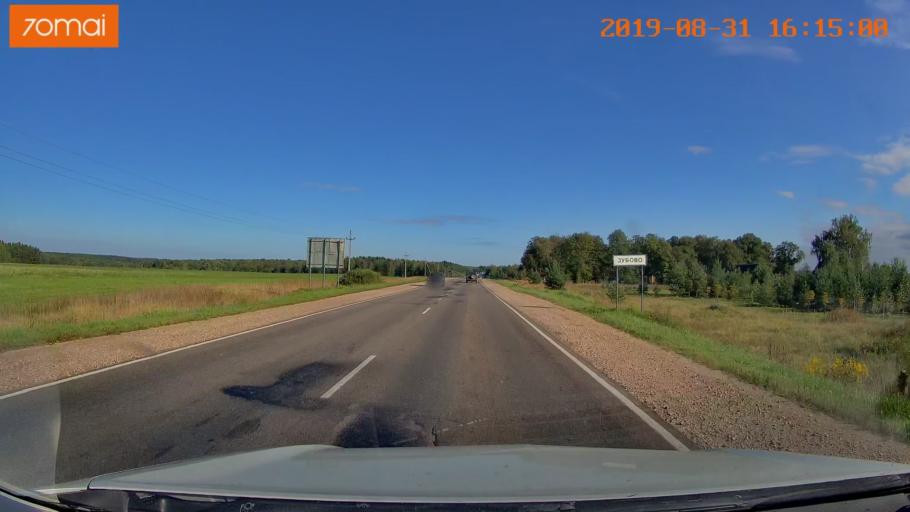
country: RU
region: Kaluga
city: Nikola-Lenivets
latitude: 54.5627
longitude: 35.4795
